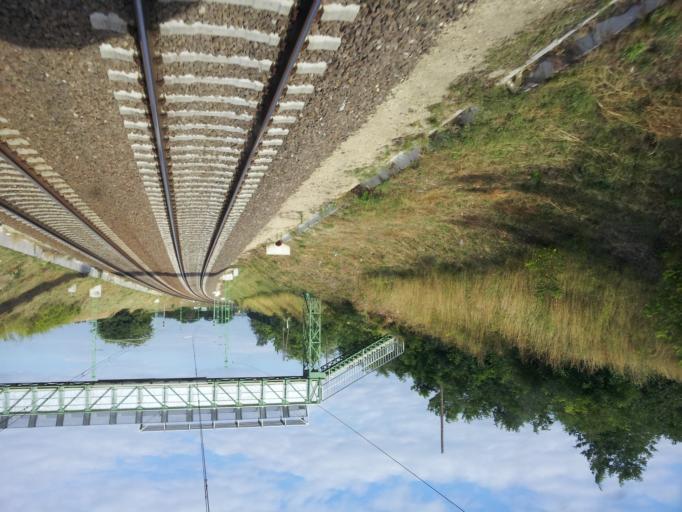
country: HU
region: Pest
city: Erd
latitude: 47.3759
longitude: 18.9001
